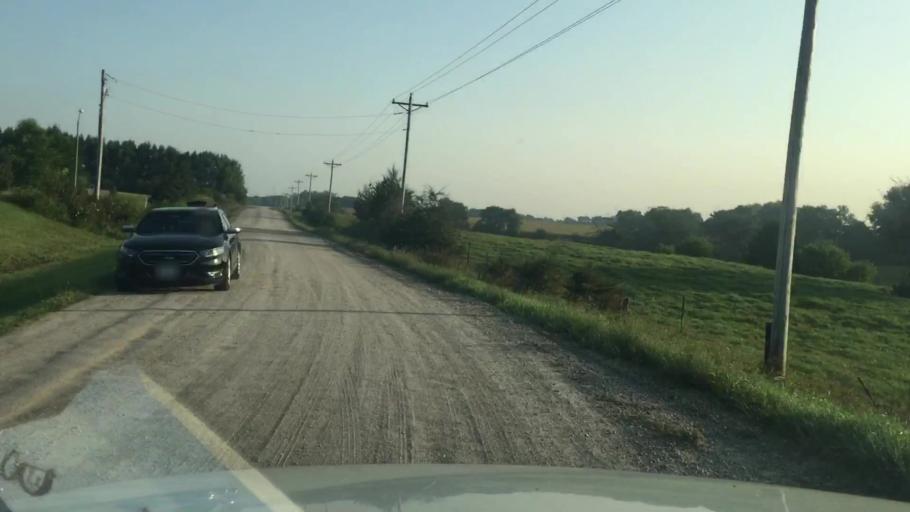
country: US
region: Iowa
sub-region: Story County
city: Huxley
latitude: 41.8935
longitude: -93.5809
